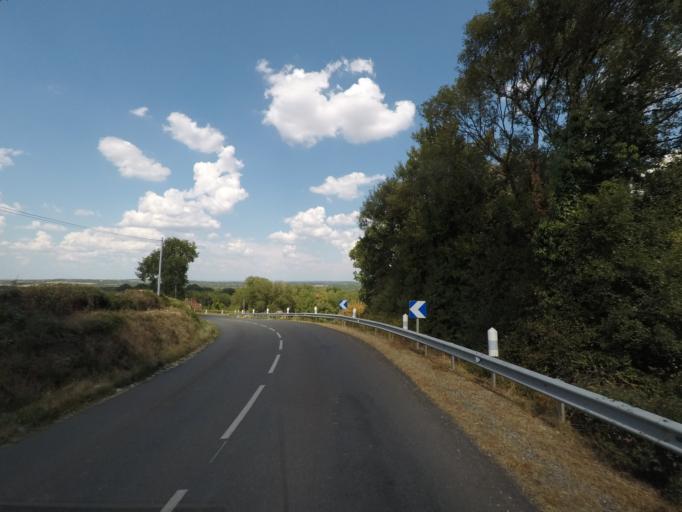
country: FR
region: Midi-Pyrenees
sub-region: Departement du Lot
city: Gramat
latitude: 44.6705
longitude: 1.5937
